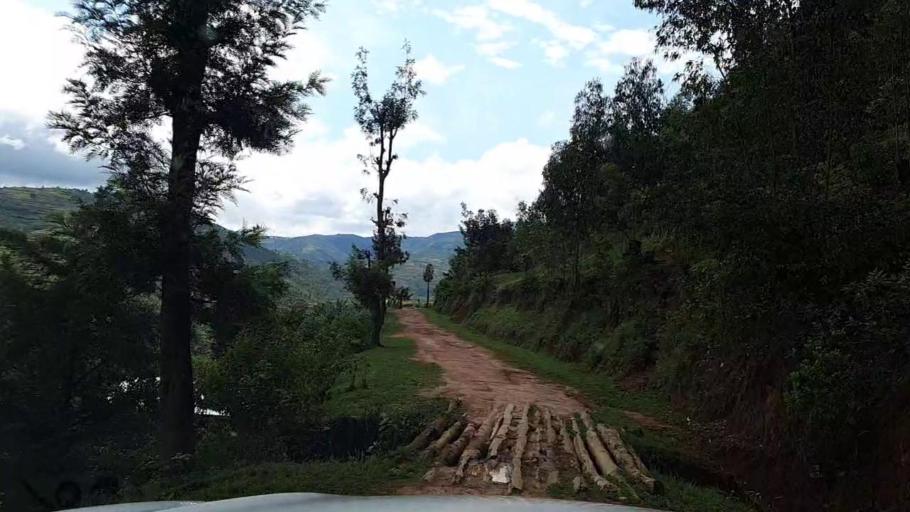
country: RW
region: Southern Province
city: Gikongoro
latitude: -2.3604
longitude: 29.5467
